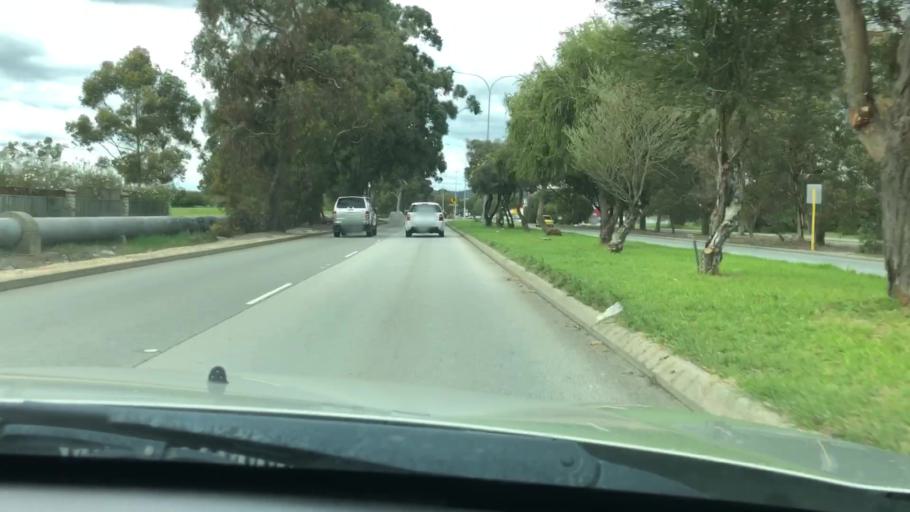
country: AU
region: Western Australia
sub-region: Armadale
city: Seville Grove
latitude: -32.1471
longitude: 115.9815
